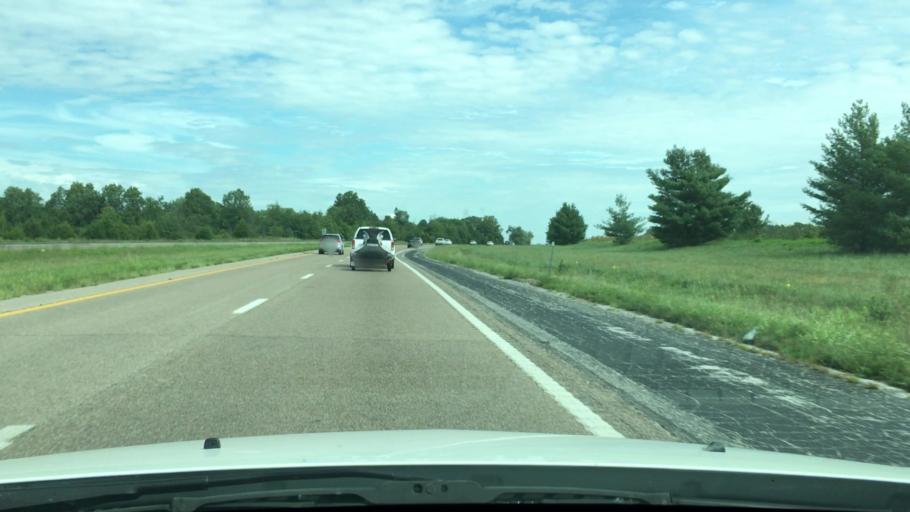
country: US
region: Missouri
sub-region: Audrain County
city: Mexico
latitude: 39.0063
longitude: -91.8929
